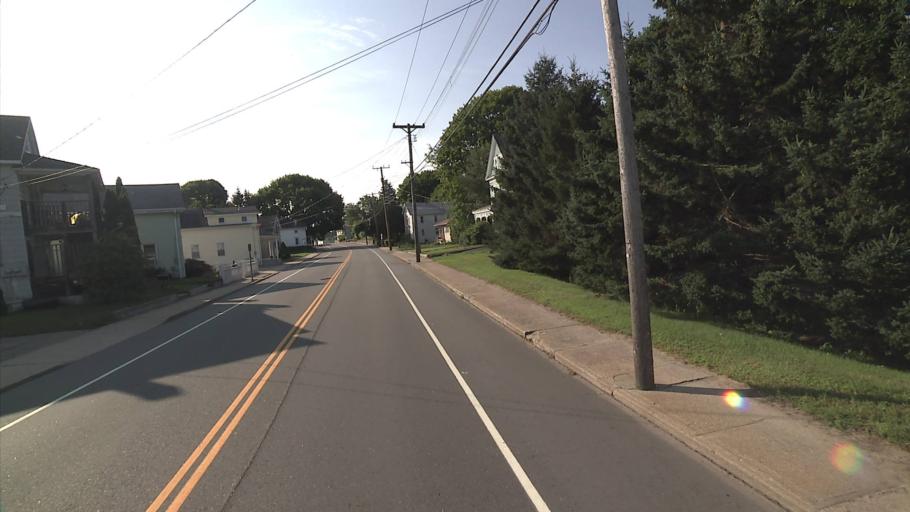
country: US
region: Connecticut
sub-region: New London County
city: Pawcatuck
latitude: 41.3830
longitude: -71.8426
